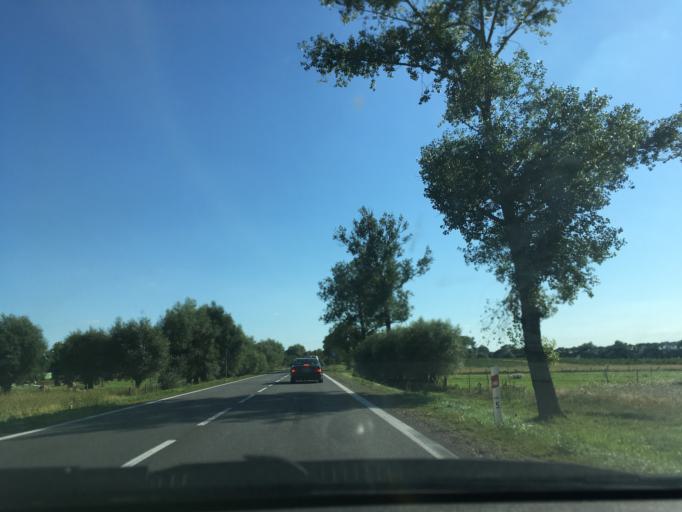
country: PL
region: Podlasie
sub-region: Powiat sokolski
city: Suchowola
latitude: 53.5172
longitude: 23.1049
